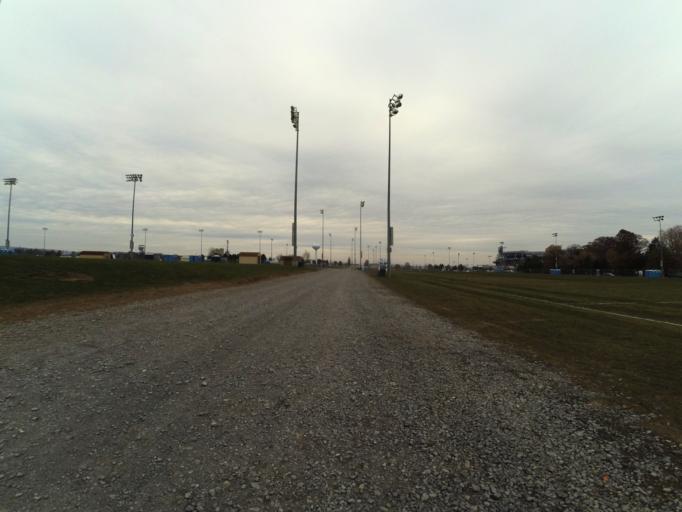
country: US
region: Pennsylvania
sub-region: Centre County
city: State College
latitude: 40.8086
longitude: -77.8644
